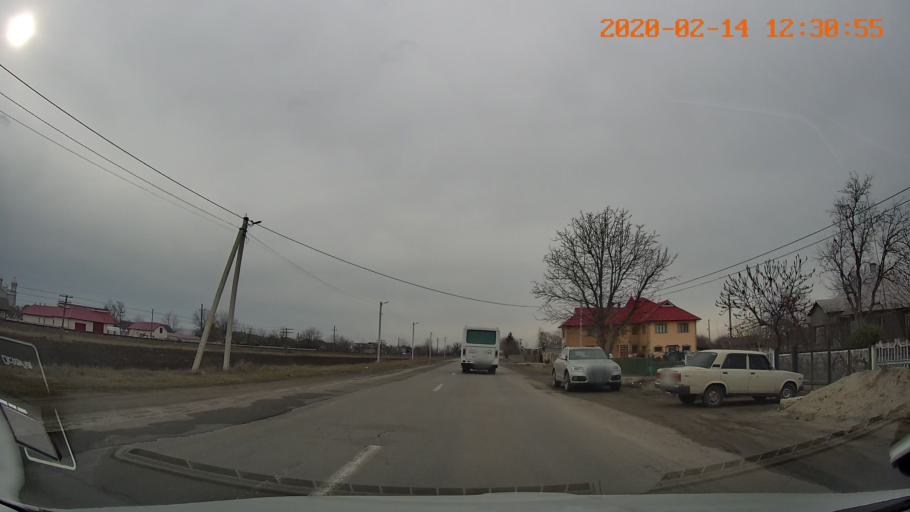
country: RO
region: Botosani
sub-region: Comuna Darabani
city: Bajura
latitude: 48.2501
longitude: 26.5613
